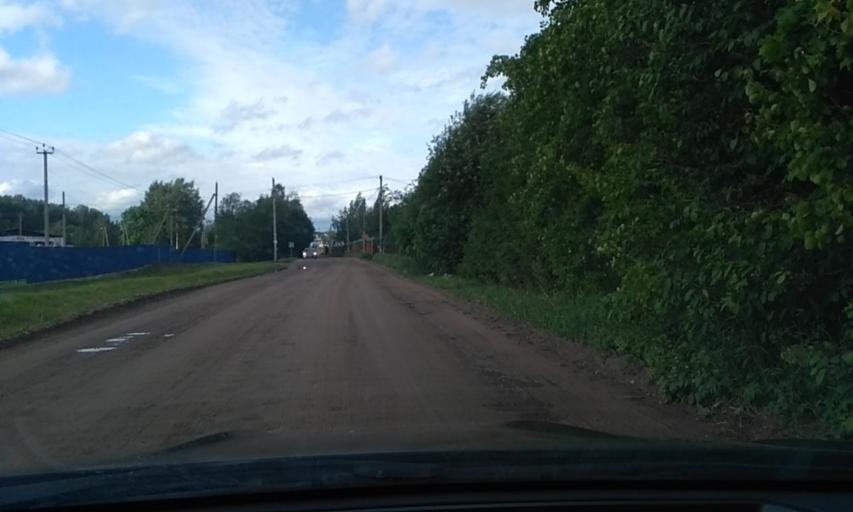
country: RU
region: Leningrad
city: Otradnoye
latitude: 59.7981
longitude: 30.8000
